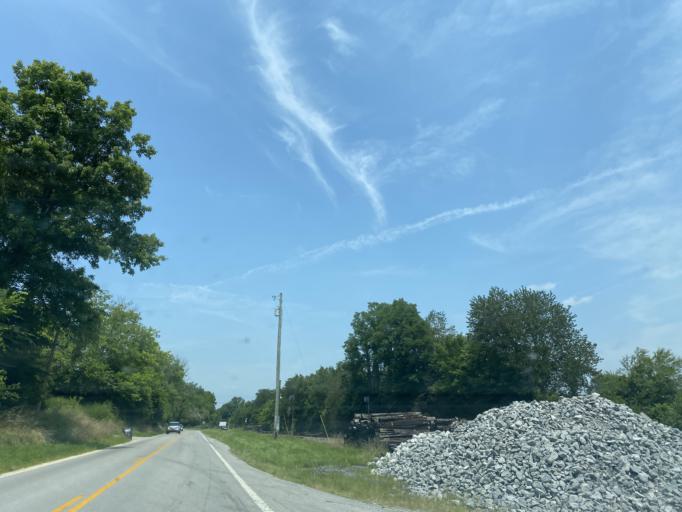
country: US
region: Kentucky
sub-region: Campbell County
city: Claryville
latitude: 38.9008
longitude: -84.4451
